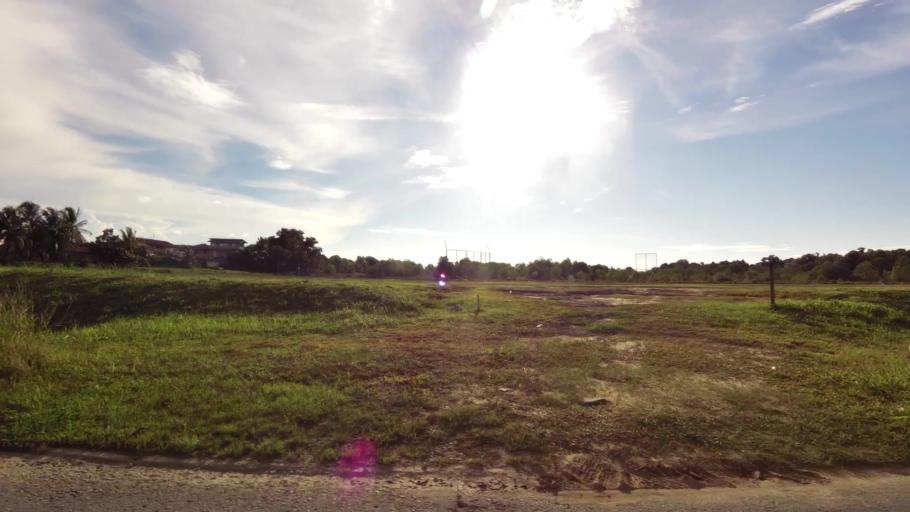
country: BN
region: Brunei and Muara
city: Bandar Seri Begawan
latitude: 4.9807
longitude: 114.9756
